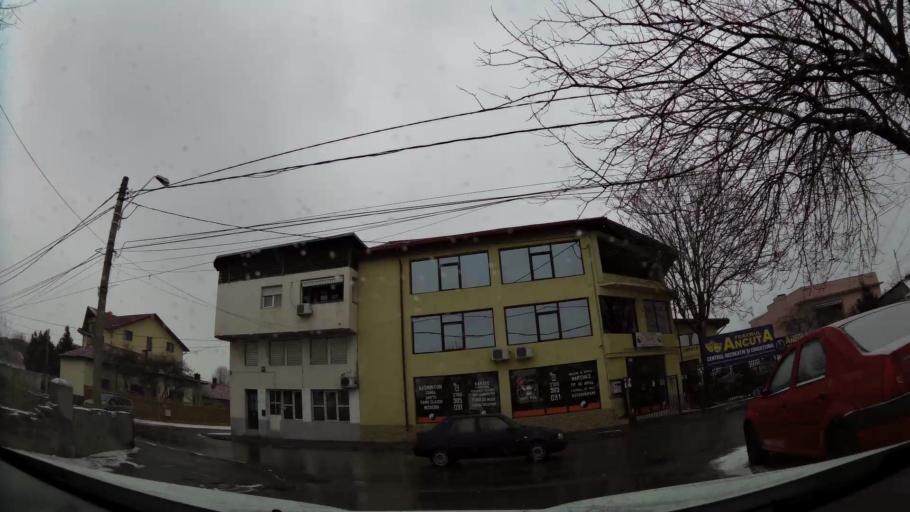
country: RO
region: Prahova
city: Ploiesti
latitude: 44.9483
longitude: 26.0239
